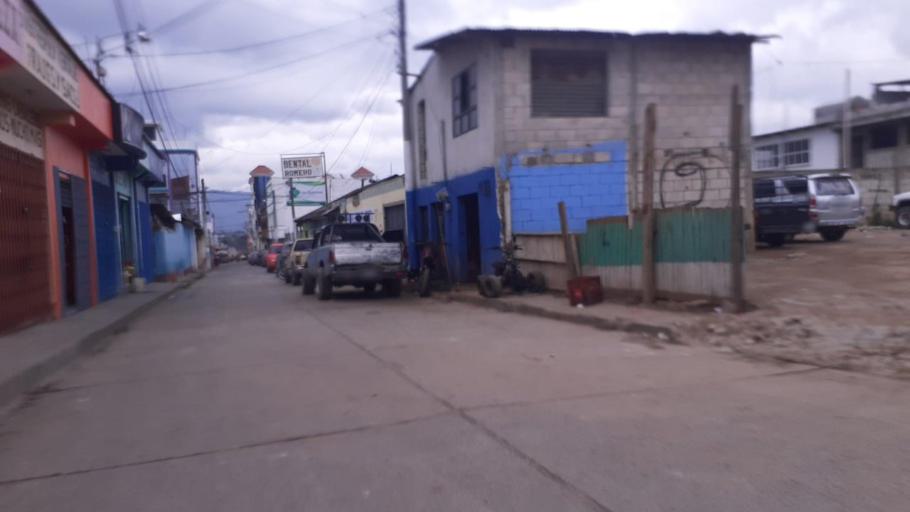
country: GT
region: Quetzaltenango
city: Ostuncalco
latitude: 14.8696
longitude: -91.6209
